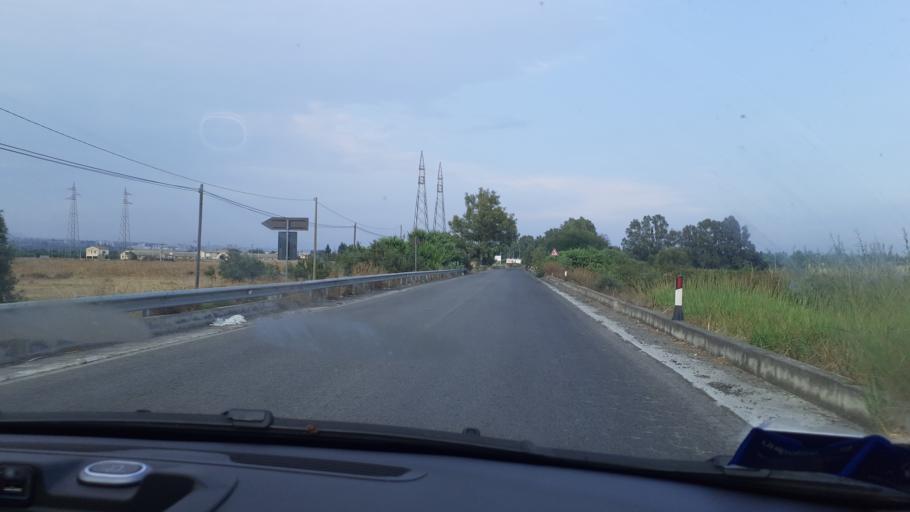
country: IT
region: Sicily
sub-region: Catania
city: Catania
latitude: 37.4481
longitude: 15.0200
